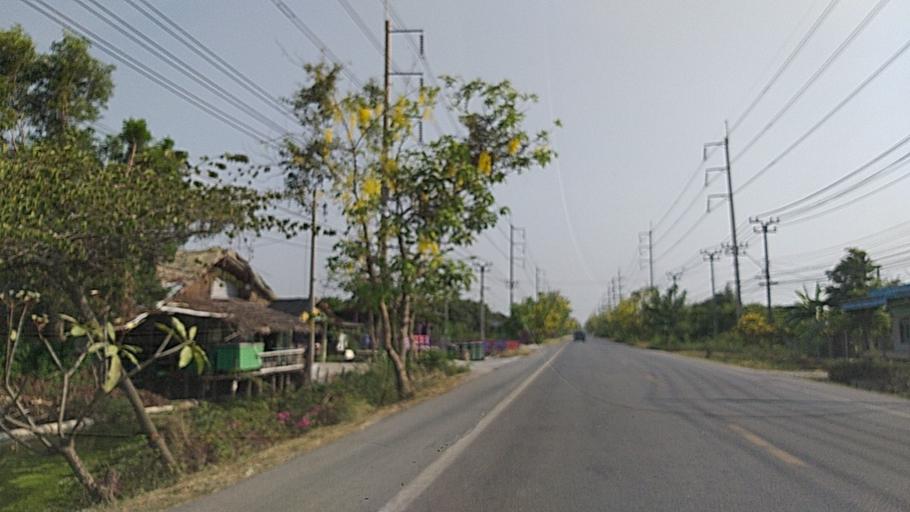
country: TH
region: Nonthaburi
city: Sai Noi
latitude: 14.0374
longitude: 100.3122
